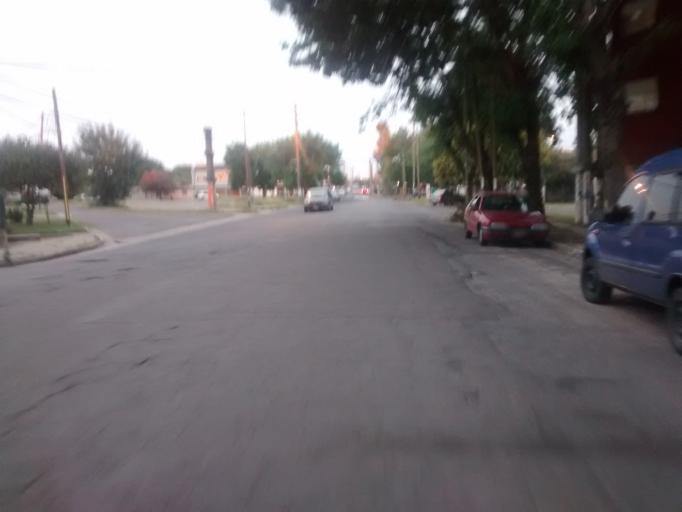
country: AR
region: Buenos Aires
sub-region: Partido de La Plata
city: La Plata
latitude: -34.9409
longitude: -57.9236
